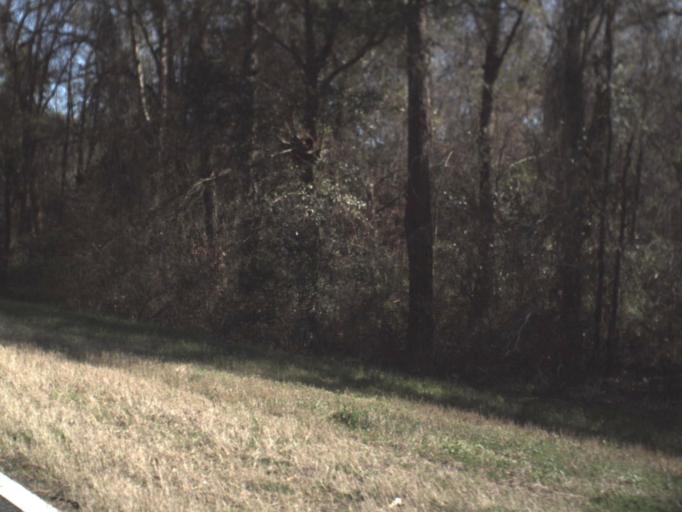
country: US
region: Florida
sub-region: Gadsden County
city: Quincy
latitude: 30.5549
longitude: -84.5270
